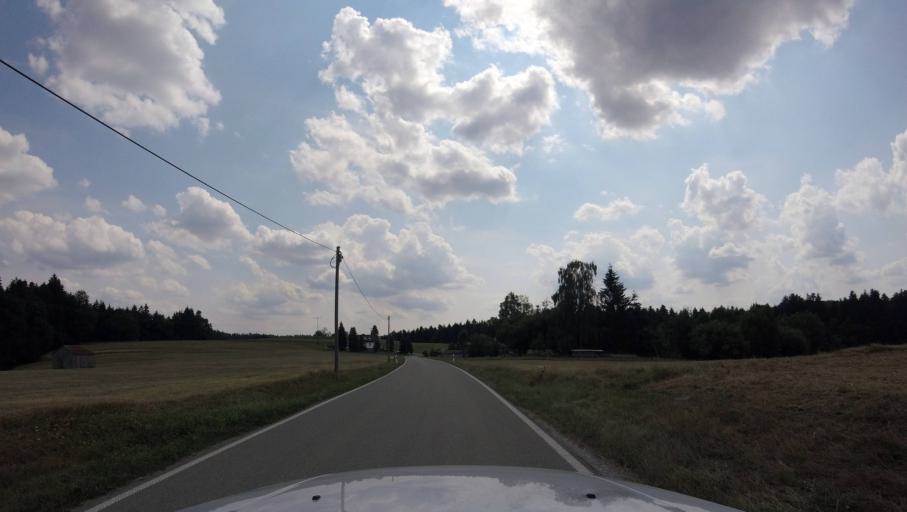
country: DE
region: Baden-Wuerttemberg
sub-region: Regierungsbezirk Stuttgart
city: Alfdorf
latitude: 48.8973
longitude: 9.6979
